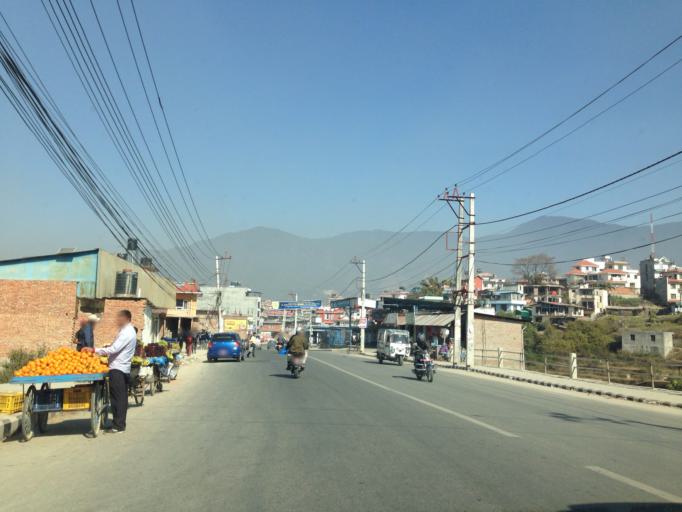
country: NP
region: Central Region
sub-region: Bagmati Zone
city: Kathmandu
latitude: 27.7489
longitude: 85.3454
